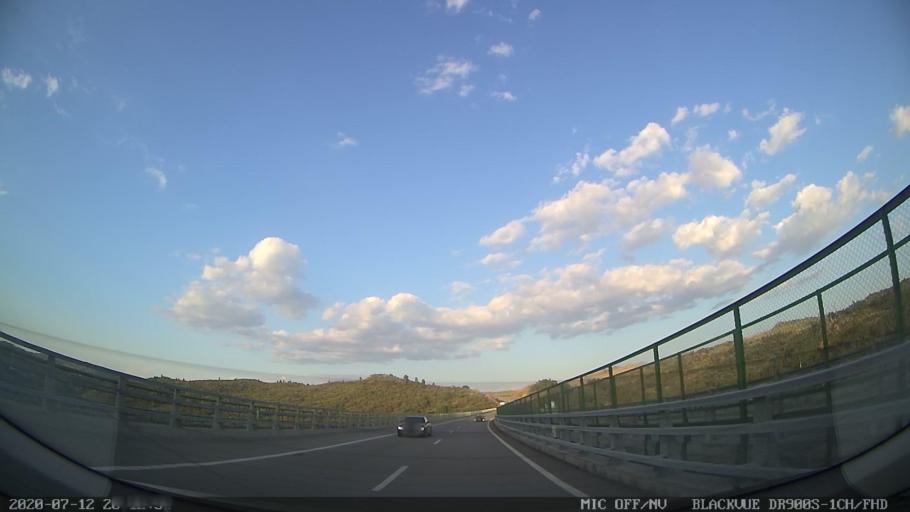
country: PT
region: Vila Real
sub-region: Sabrosa
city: Sabrosa
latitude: 41.3605
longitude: -7.5747
